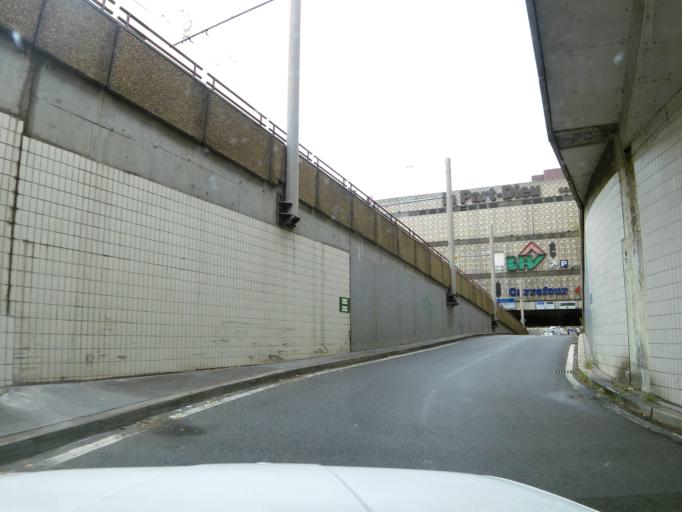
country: FR
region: Rhone-Alpes
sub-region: Departement du Rhone
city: Lyon
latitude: 45.7616
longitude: 4.8587
